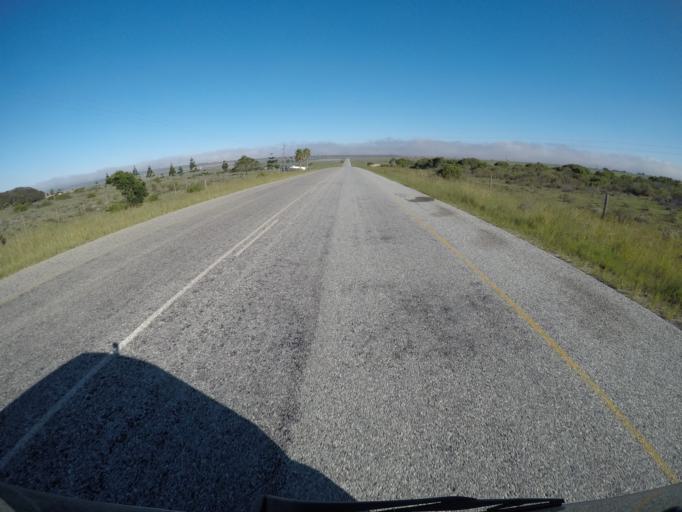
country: ZA
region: Western Cape
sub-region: Eden District Municipality
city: Mossel Bay
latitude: -34.1673
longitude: 22.0124
